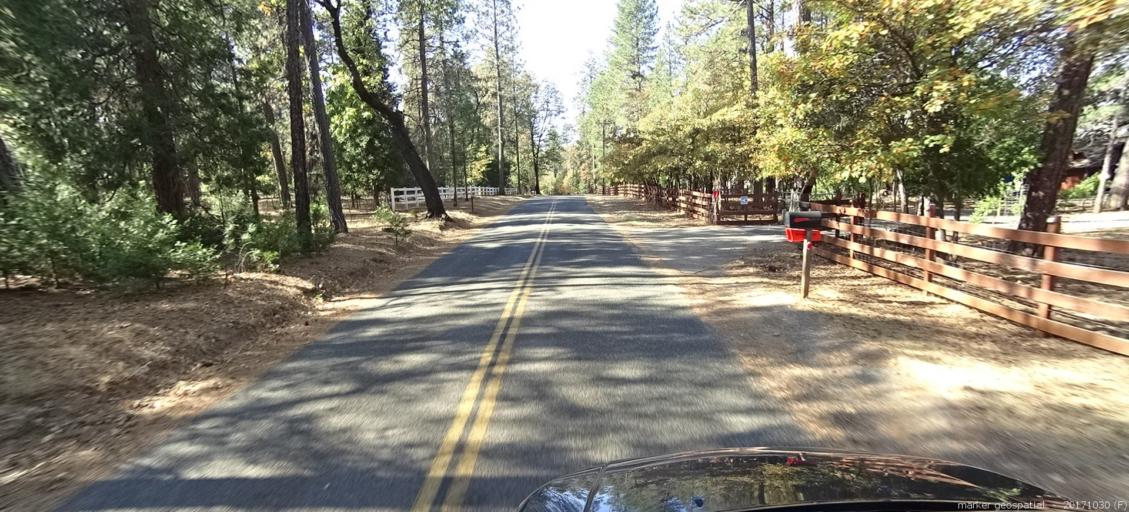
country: US
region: California
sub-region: Shasta County
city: Shingletown
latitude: 40.6027
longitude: -121.9610
